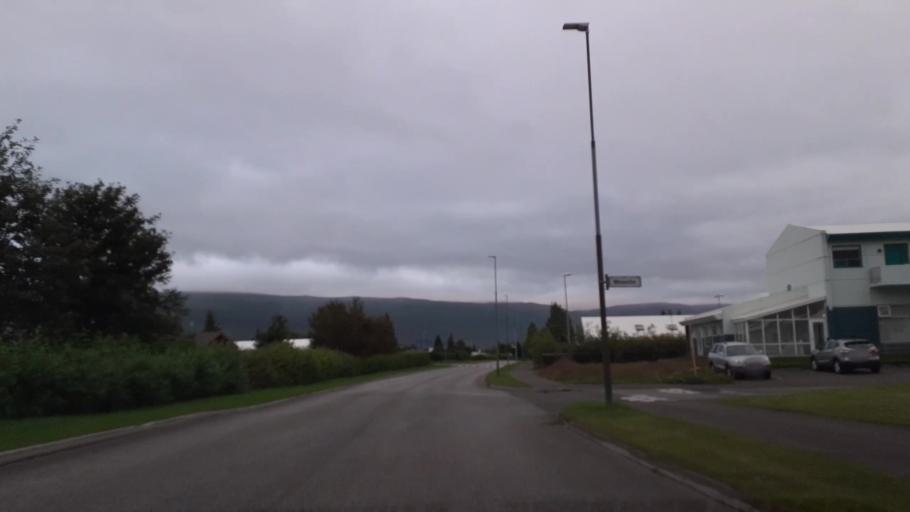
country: IS
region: Northeast
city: Akureyri
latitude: 65.6960
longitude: -18.1418
